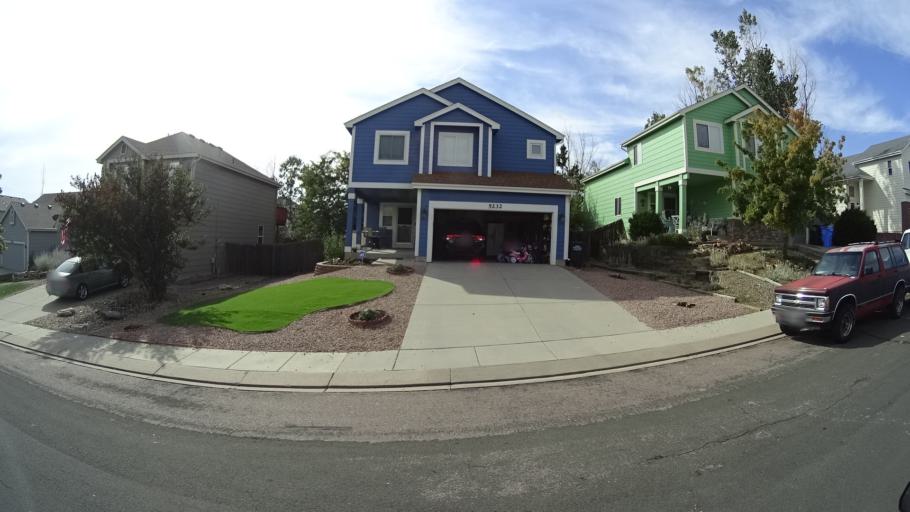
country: US
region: Colorado
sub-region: El Paso County
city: Cimarron Hills
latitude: 38.9076
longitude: -104.6957
